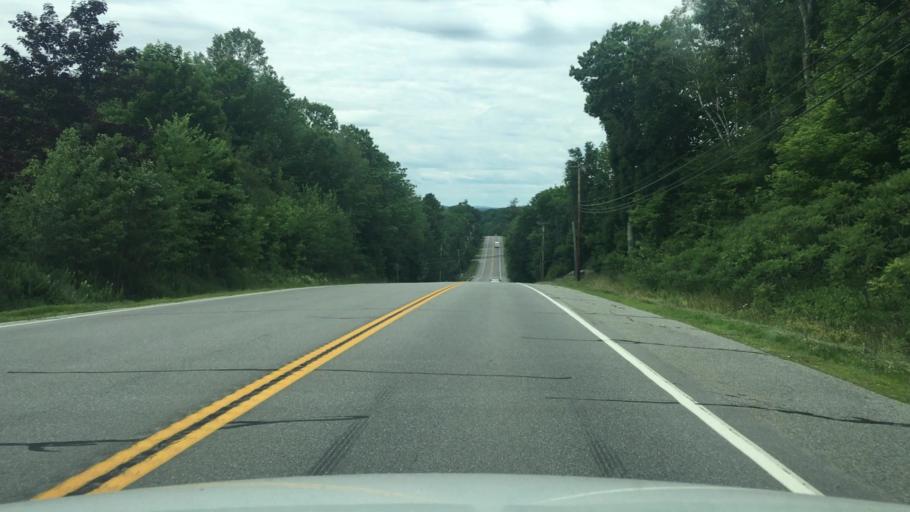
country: US
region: Maine
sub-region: Kennebec County
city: Sidney
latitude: 44.3354
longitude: -69.6899
